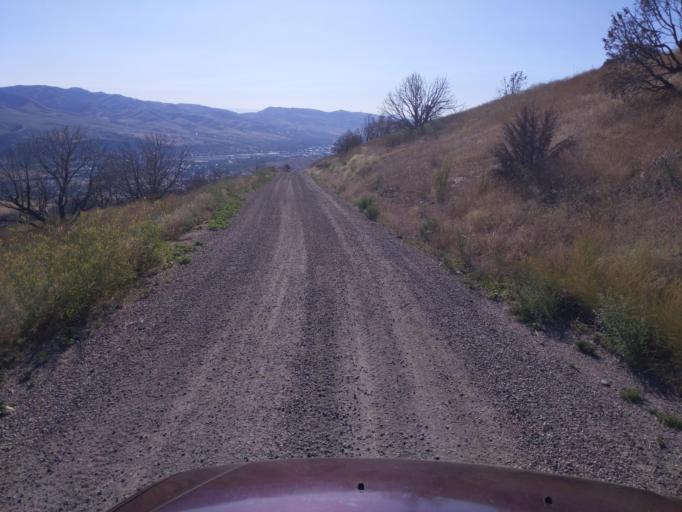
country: US
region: Idaho
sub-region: Bannock County
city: Pocatello
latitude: 42.8495
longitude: -112.3758
